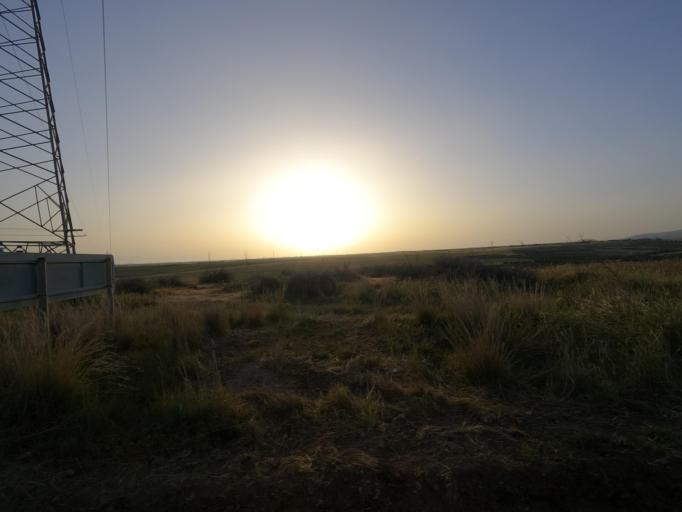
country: CY
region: Lefkosia
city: Astromeritis
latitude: 35.1203
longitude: 33.0146
